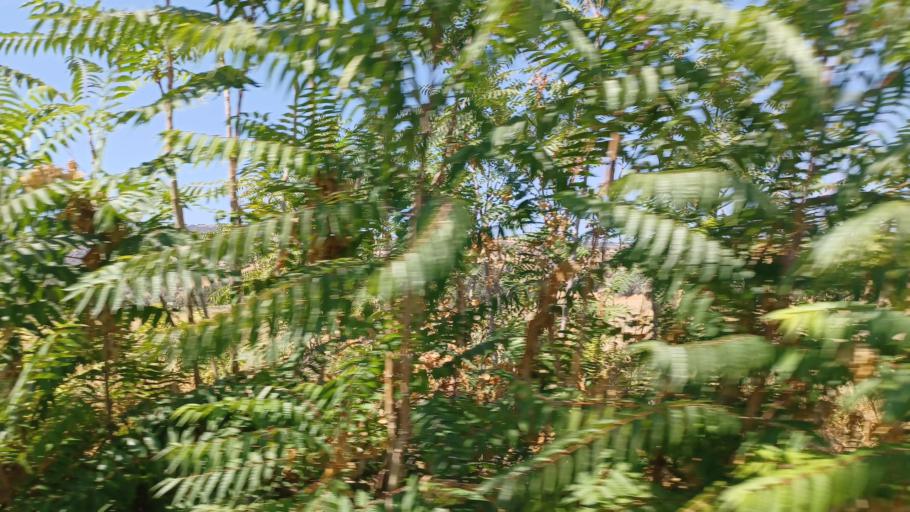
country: CY
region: Pafos
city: Polis
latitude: 35.0134
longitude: 32.4346
